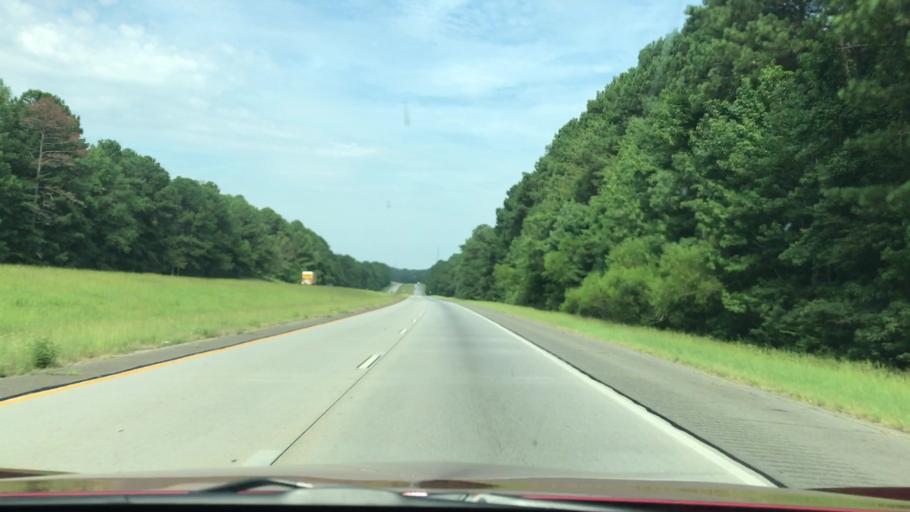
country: US
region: Georgia
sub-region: Warren County
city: Firing Range
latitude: 33.5044
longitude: -82.7518
